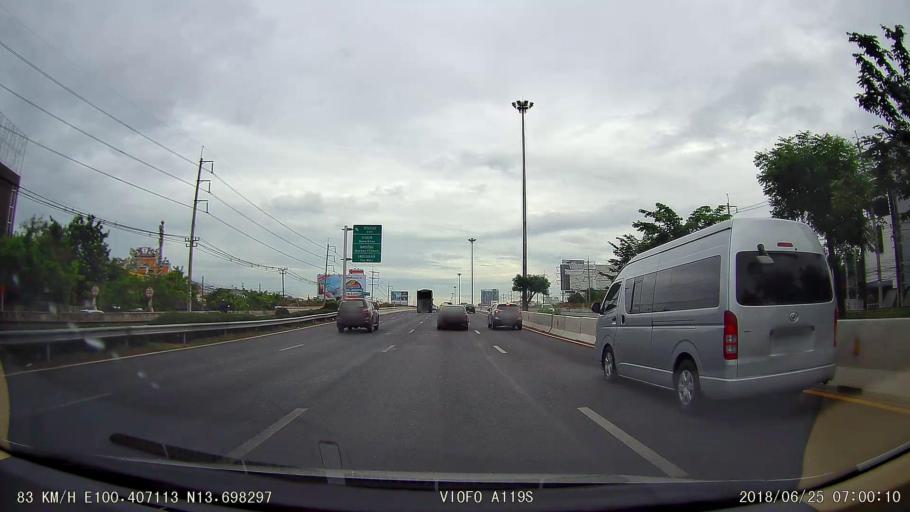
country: TH
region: Bangkok
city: Bang Khae
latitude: 13.6979
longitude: 100.4072
